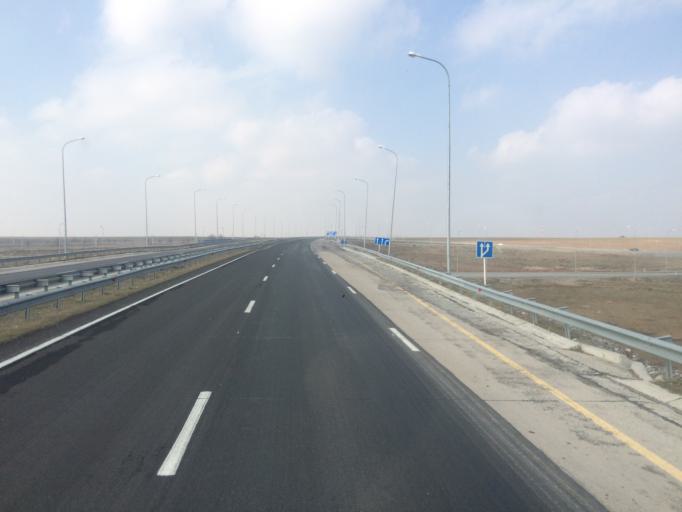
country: KZ
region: Ongtustik Qazaqstan
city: Temirlanovka
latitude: 42.5277
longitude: 69.3474
